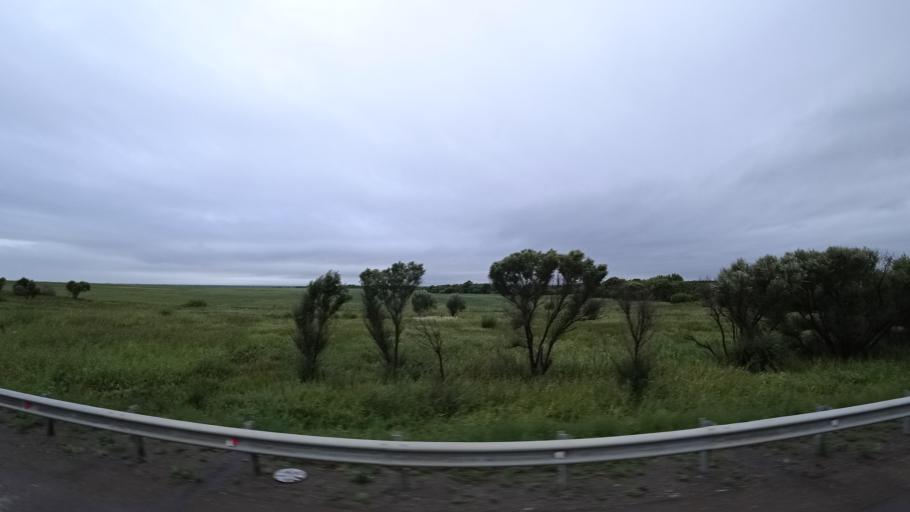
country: RU
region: Primorskiy
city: Chernigovka
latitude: 44.3088
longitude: 132.5428
